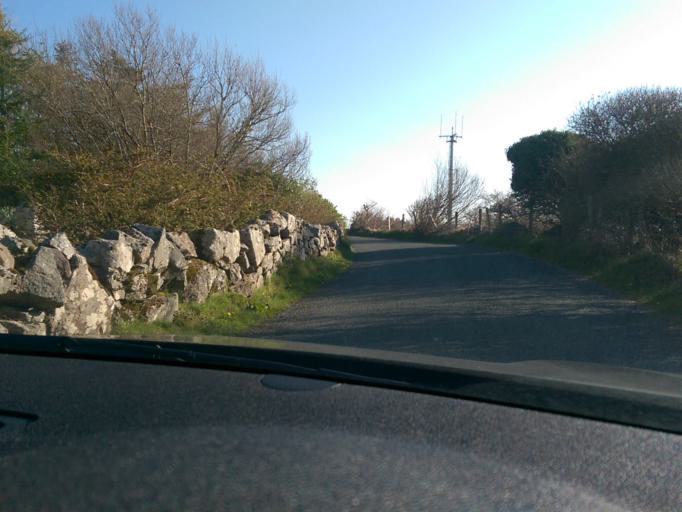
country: IE
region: Connaught
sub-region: County Galway
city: Clifden
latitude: 53.4231
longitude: -9.8270
